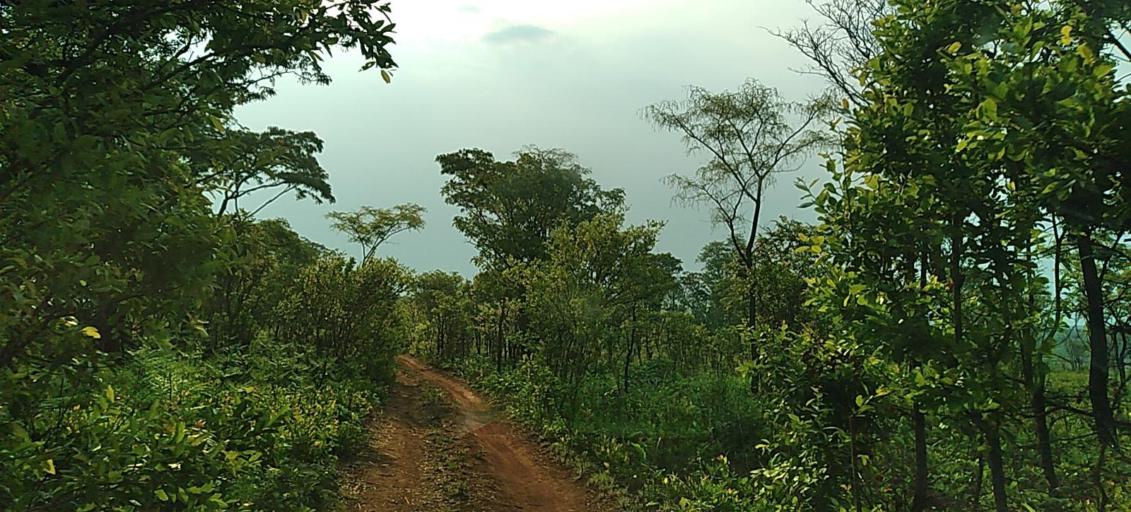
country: ZM
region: North-Western
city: Solwezi
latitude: -12.0432
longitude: 26.0509
